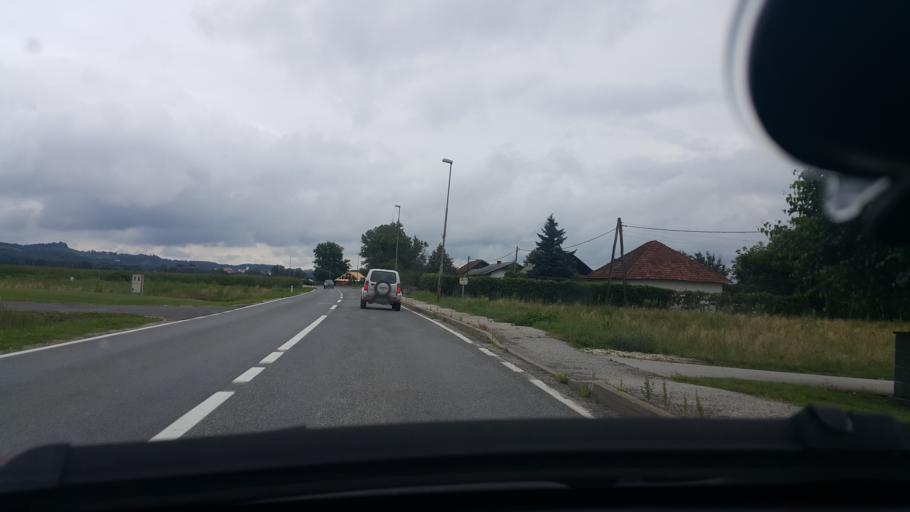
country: SI
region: Zavrc
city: Zavrc
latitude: 46.4153
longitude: 16.0740
